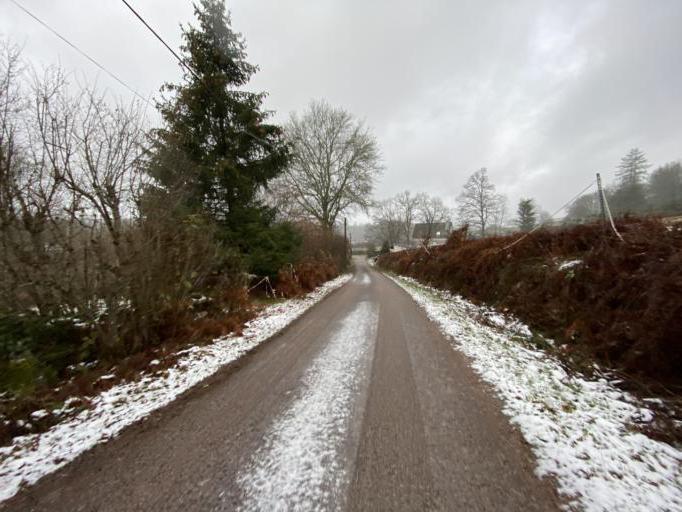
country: FR
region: Bourgogne
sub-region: Departement de la Cote-d'Or
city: Saulieu
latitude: 47.2679
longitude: 4.1564
